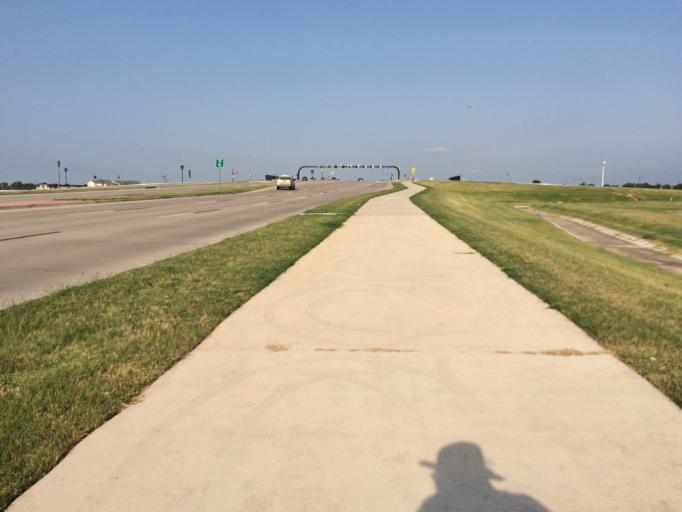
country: US
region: Oklahoma
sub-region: Cleveland County
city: Norman
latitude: 35.2186
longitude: -97.4822
